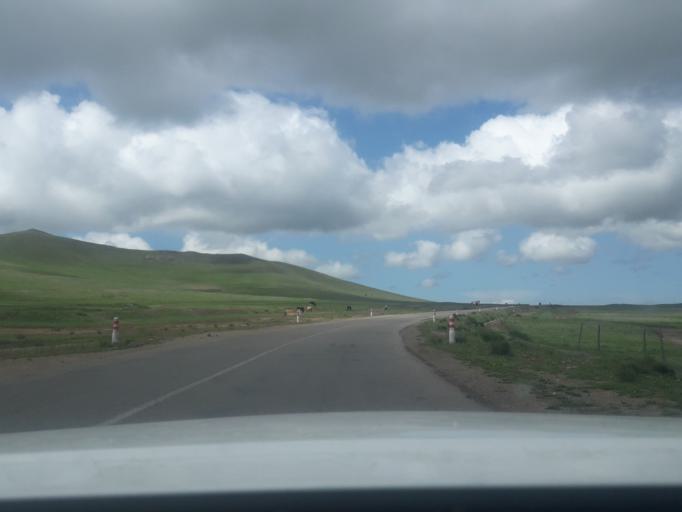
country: MN
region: Central Aimak
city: Altanbulag
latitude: 47.8996
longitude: 106.4198
